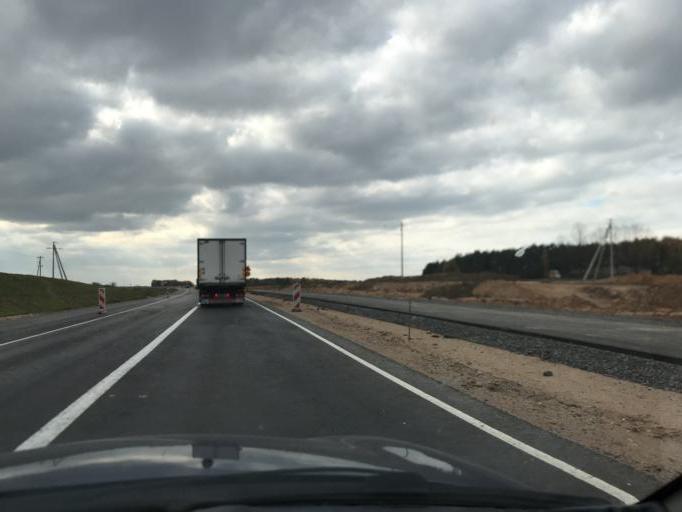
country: BY
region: Grodnenskaya
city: Lida
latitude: 53.8237
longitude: 25.1270
